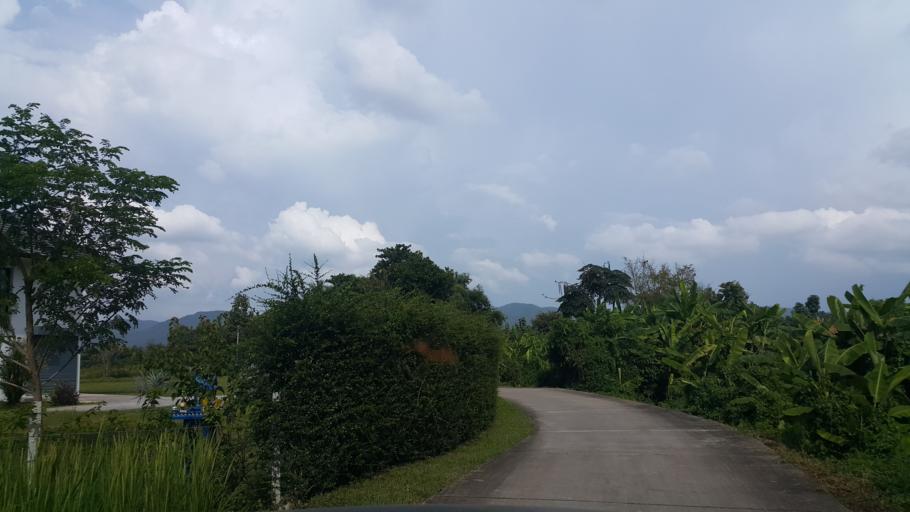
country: TH
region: Chiang Mai
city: San Sai
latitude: 18.8983
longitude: 99.1246
